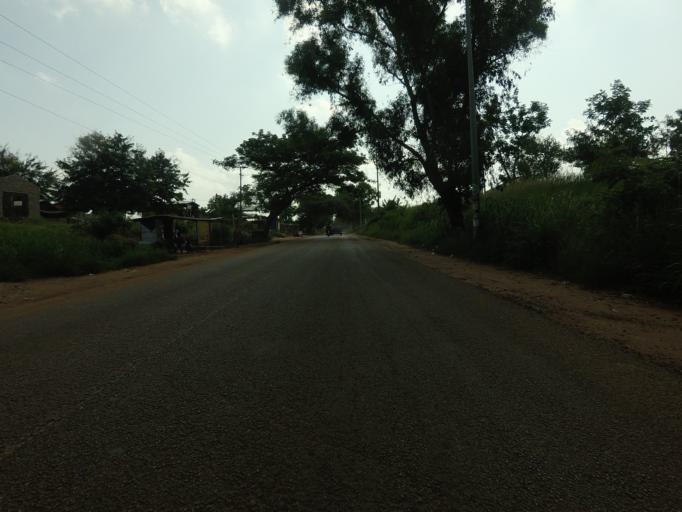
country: GH
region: Volta
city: Ho
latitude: 6.6011
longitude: 0.4989
